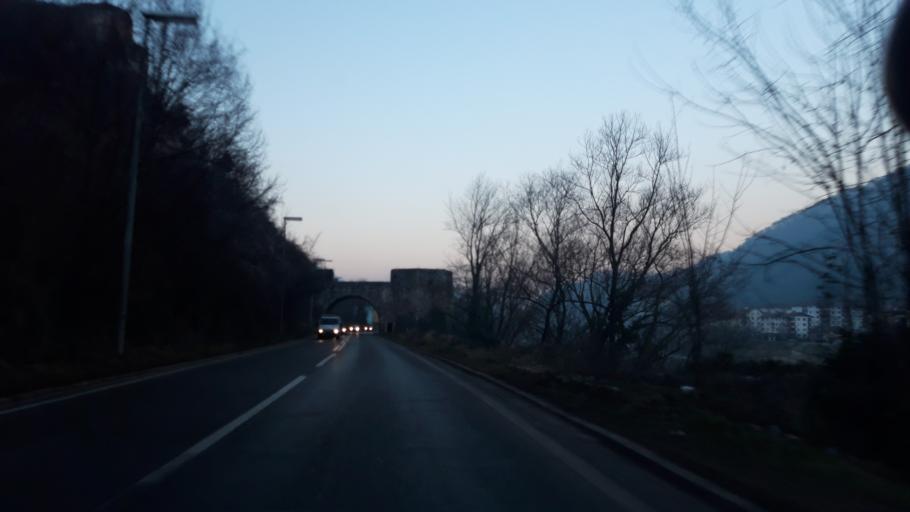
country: RS
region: Central Serbia
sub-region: Macvanski Okrug
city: Mali Zvornik
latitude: 44.3732
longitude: 19.1016
